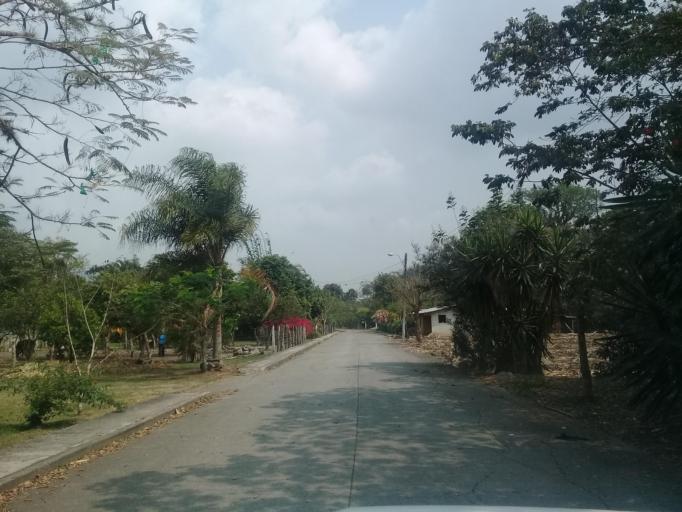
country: MX
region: Veracruz
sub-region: Ixtaczoquitlan
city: Capoluca
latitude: 18.8182
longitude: -96.9914
